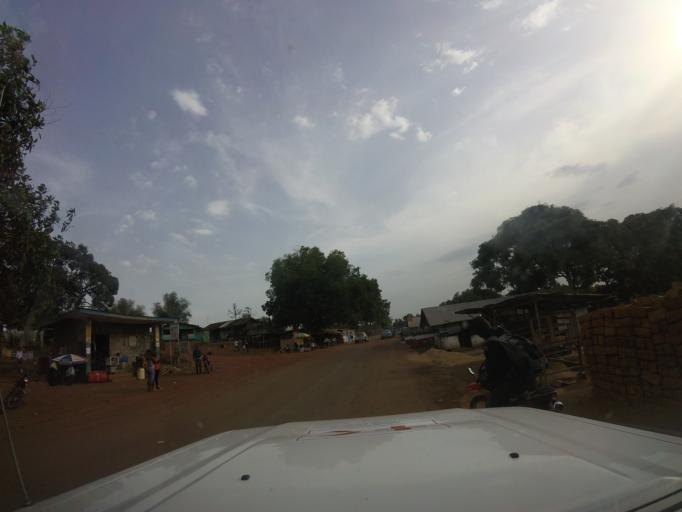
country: LR
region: Grand Cape Mount
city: Robertsport
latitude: 6.8158
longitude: -11.1371
